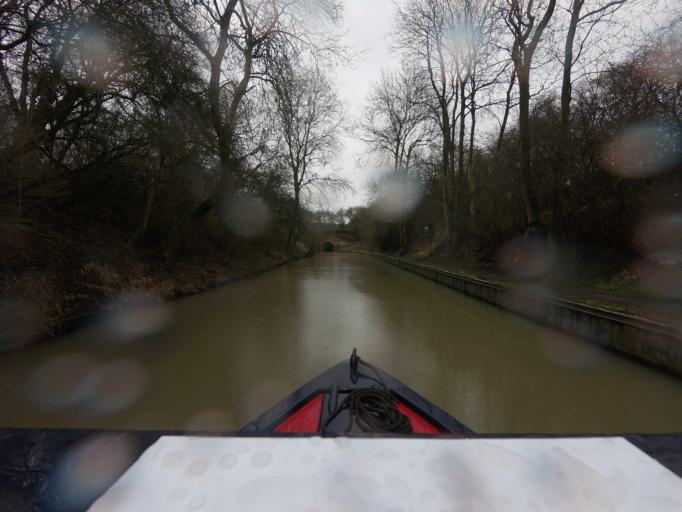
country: GB
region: England
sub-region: Northamptonshire
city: Daventry
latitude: 52.2850
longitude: -1.1861
